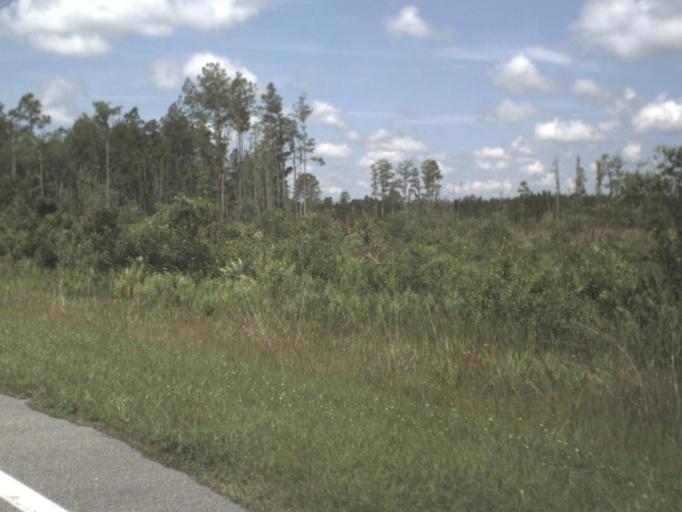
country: US
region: Florida
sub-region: Levy County
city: Bronson
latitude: 29.4094
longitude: -82.6854
